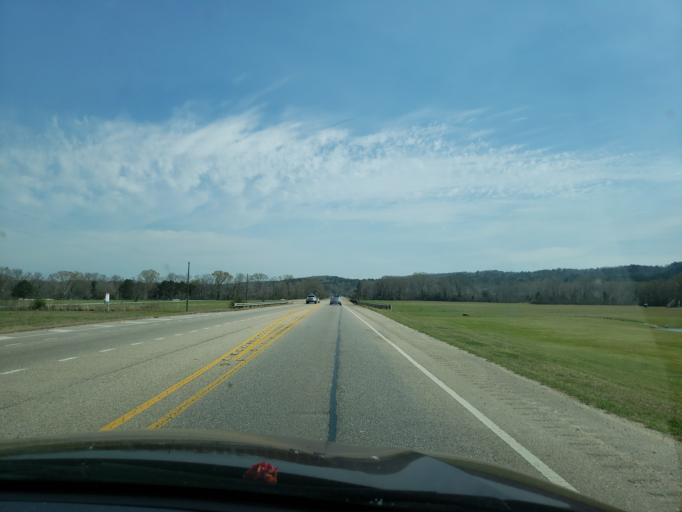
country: US
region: Alabama
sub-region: Elmore County
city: Wetumpka
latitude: 32.5523
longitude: -86.2028
